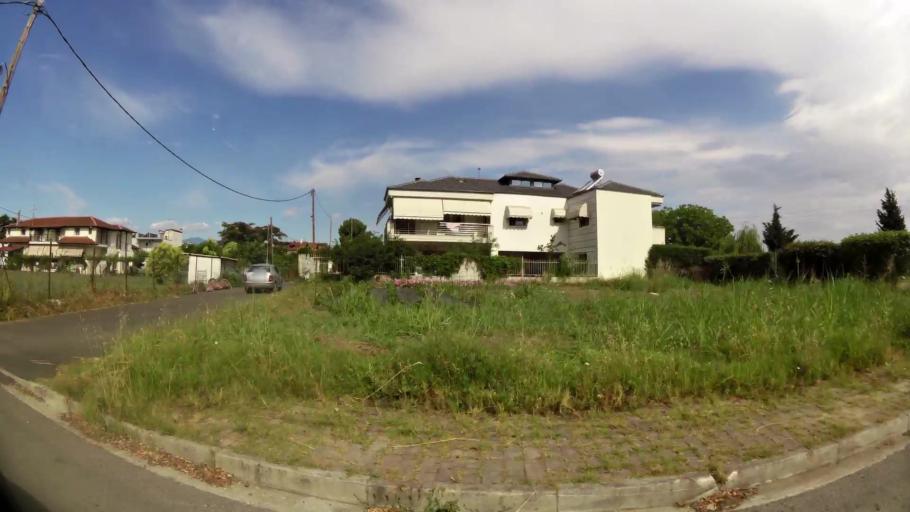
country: GR
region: Central Macedonia
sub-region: Nomos Pierias
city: Katerini
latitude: 40.2848
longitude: 22.5163
